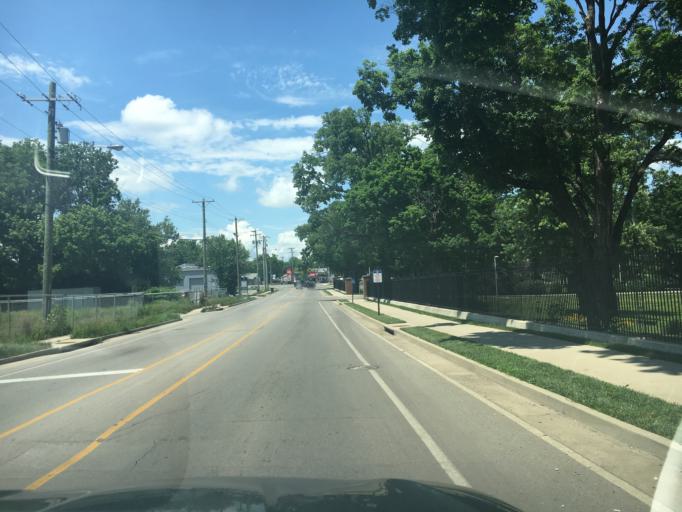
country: US
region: Kentucky
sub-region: Fayette County
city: Mount Vernon
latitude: 38.0588
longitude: -84.4991
